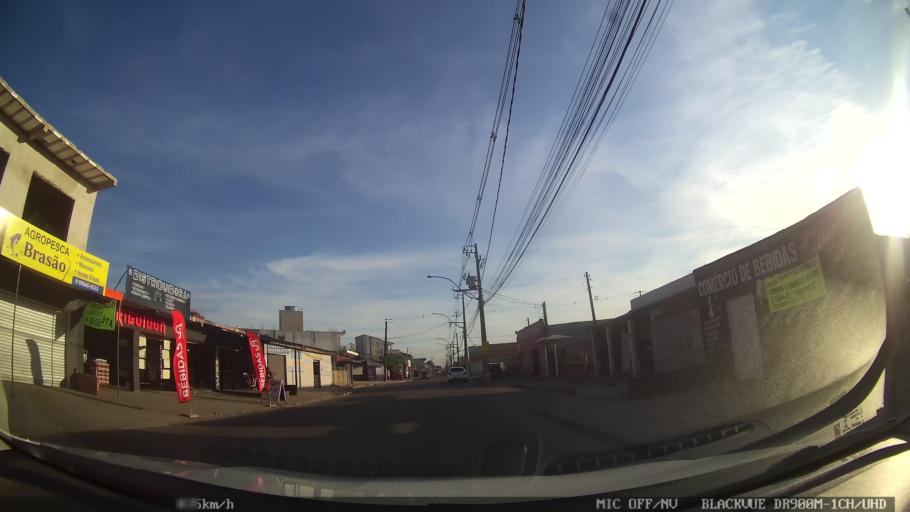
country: BR
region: Parana
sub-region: Pinhais
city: Pinhais
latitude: -25.4482
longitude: -49.1426
